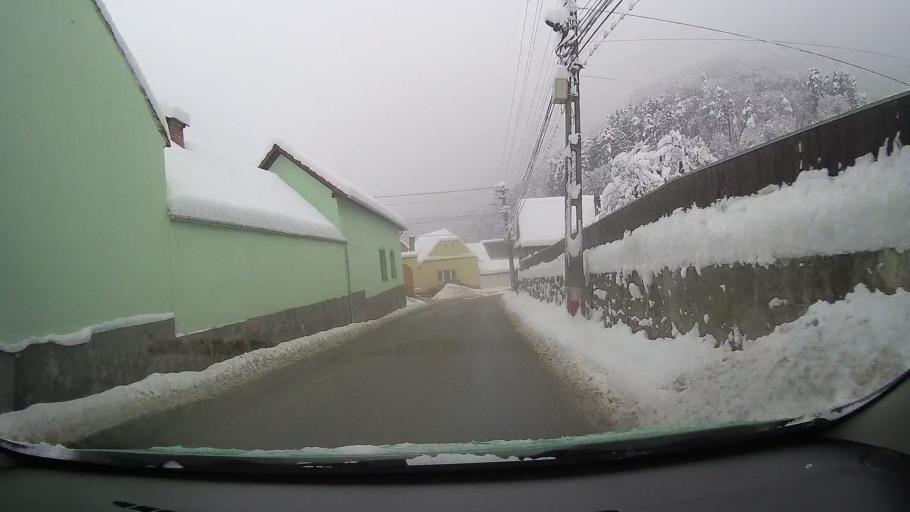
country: RO
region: Sibiu
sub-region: Comuna Tilisca
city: Tilisca
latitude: 45.7987
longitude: 23.8635
